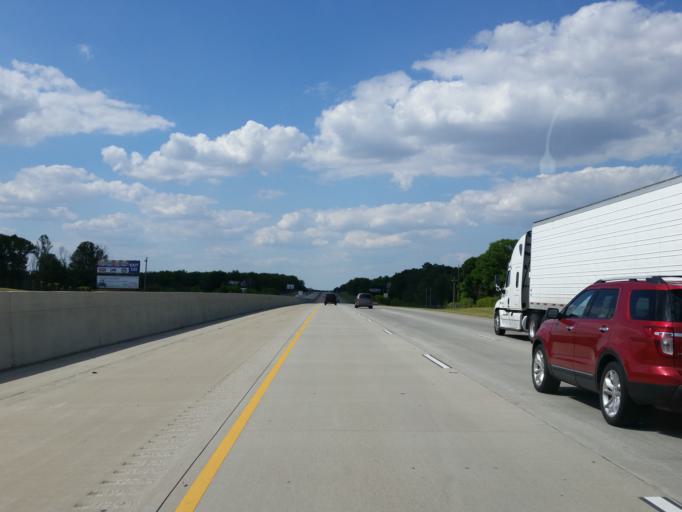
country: US
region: Georgia
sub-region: Crisp County
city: Cordele
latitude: 32.0121
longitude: -83.7597
